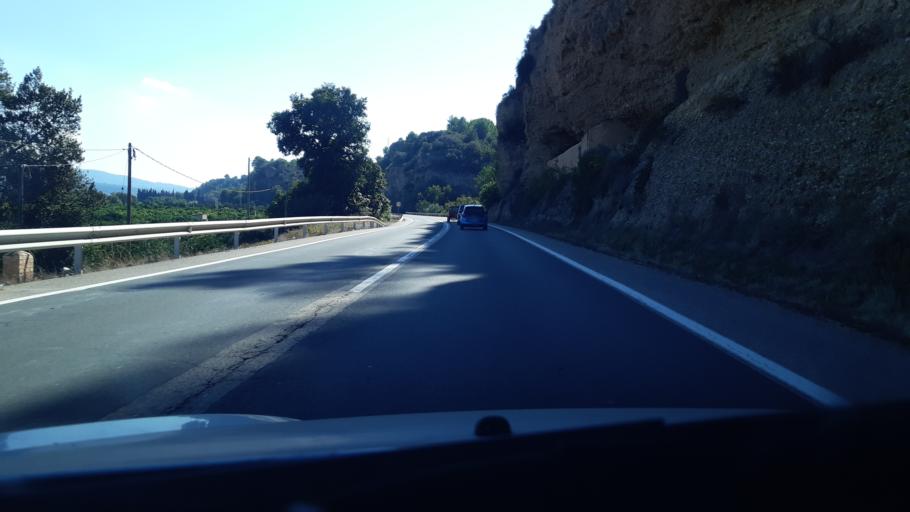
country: ES
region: Catalonia
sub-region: Provincia de Tarragona
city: Tivenys
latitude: 40.8729
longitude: 0.5012
